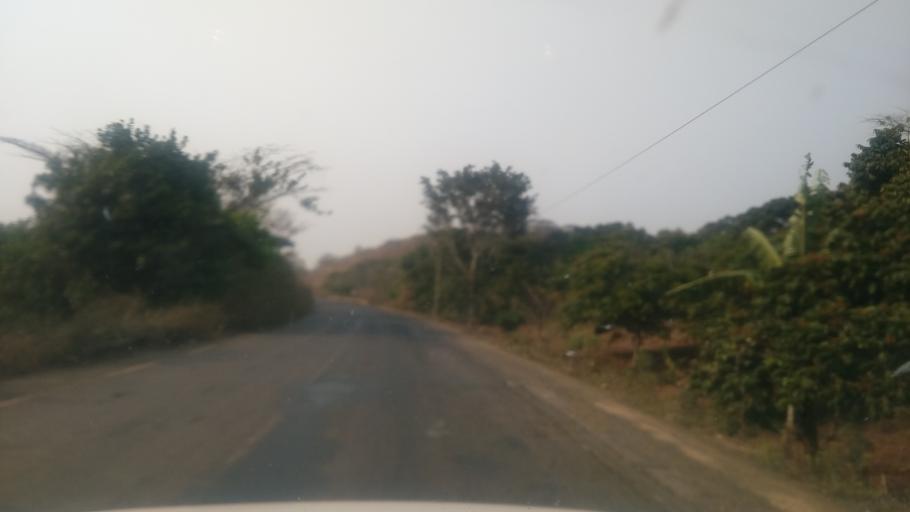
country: CM
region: West
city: Tonga
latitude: 5.0522
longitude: 10.6992
